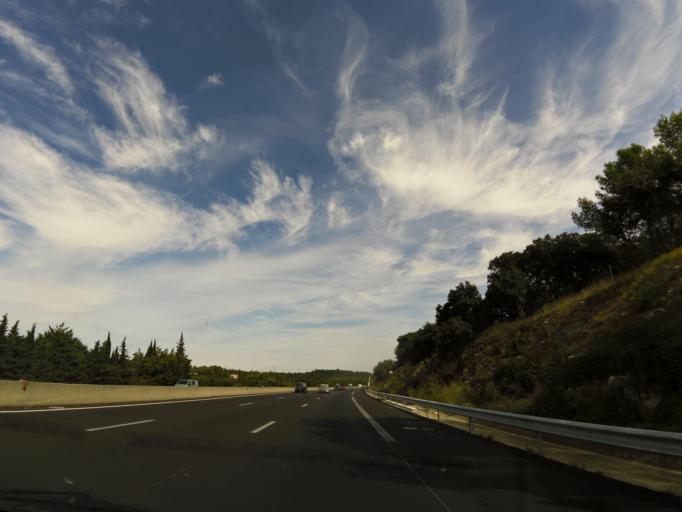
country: FR
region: Languedoc-Roussillon
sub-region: Departement du Gard
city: Uchaud
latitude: 43.7661
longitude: 4.2682
